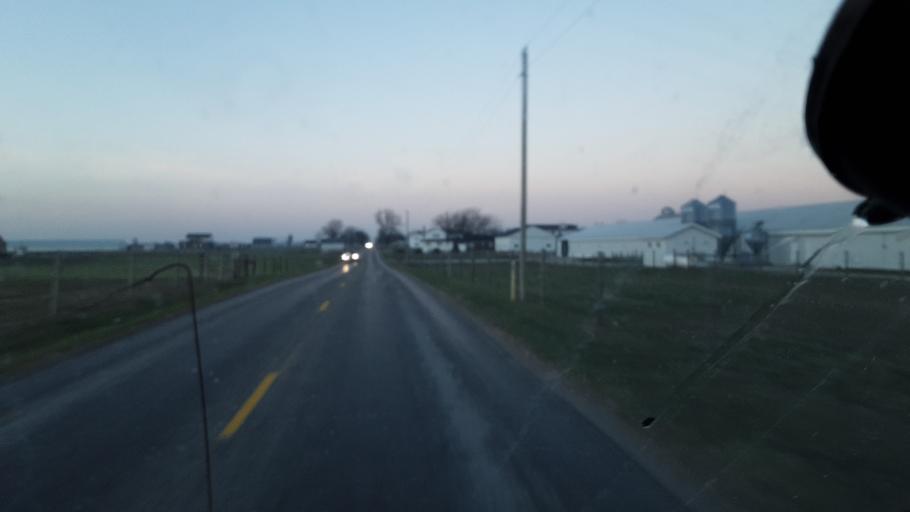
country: US
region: Indiana
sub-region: Allen County
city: Grabill
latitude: 41.2313
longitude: -84.9426
